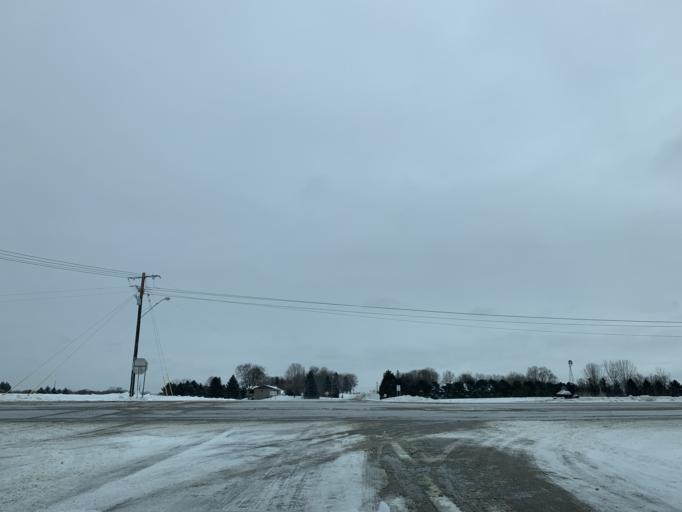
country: US
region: Minnesota
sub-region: Carver County
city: Carver
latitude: 44.7911
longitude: -93.6427
